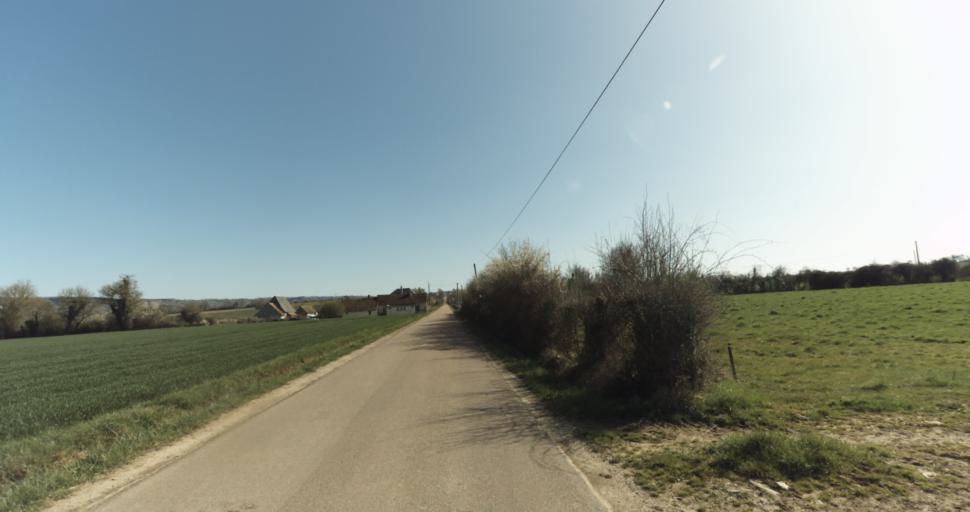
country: FR
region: Lower Normandy
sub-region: Departement du Calvados
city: Saint-Pierre-sur-Dives
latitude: 48.9496
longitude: 0.0133
